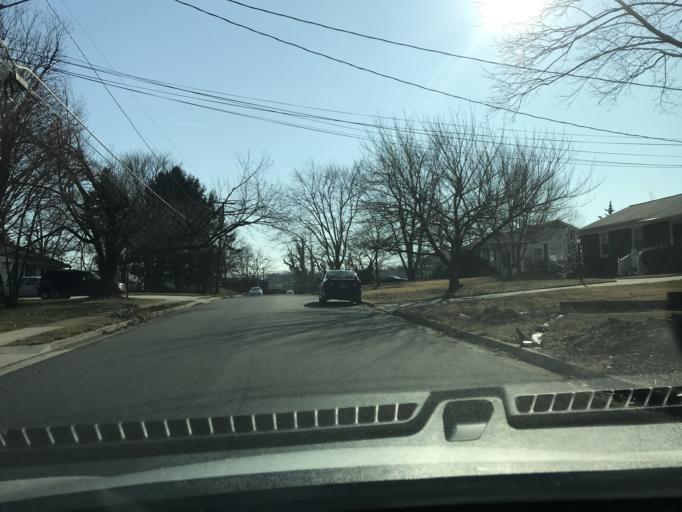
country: US
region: Virginia
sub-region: City of Fairfax
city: Fairfax
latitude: 38.8554
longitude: -77.3225
